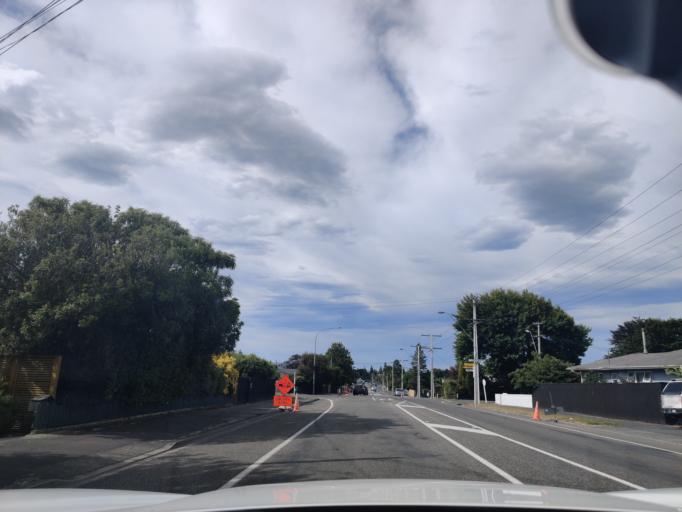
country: NZ
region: Wellington
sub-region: Masterton District
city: Masterton
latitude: -40.9388
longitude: 175.6705
